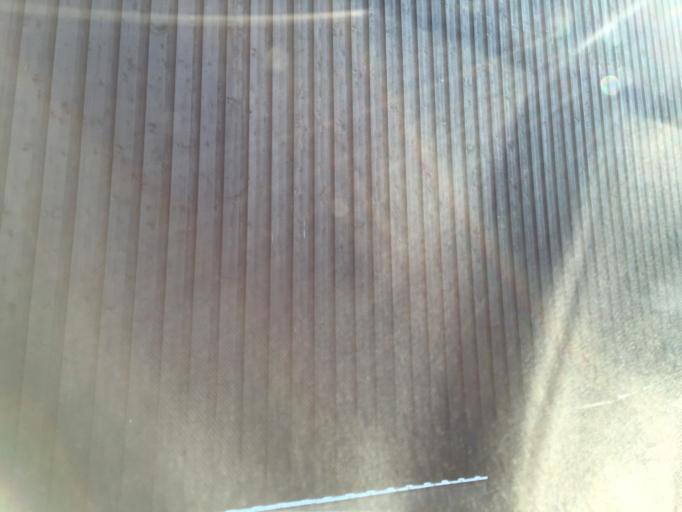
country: EE
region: Saare
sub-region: Kuressaare linn
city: Kuressaare
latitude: 58.2547
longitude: 22.4879
